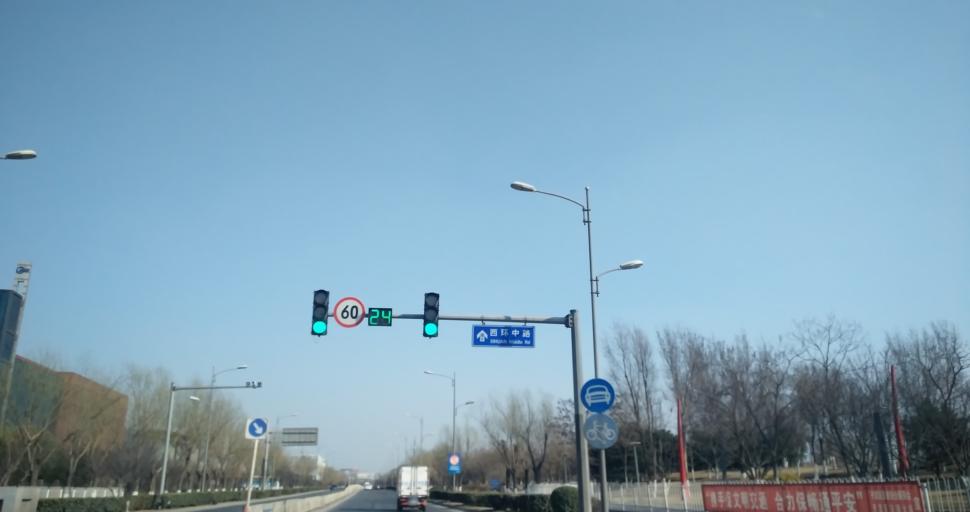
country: CN
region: Beijing
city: Jiugong
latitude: 39.7766
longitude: 116.4987
